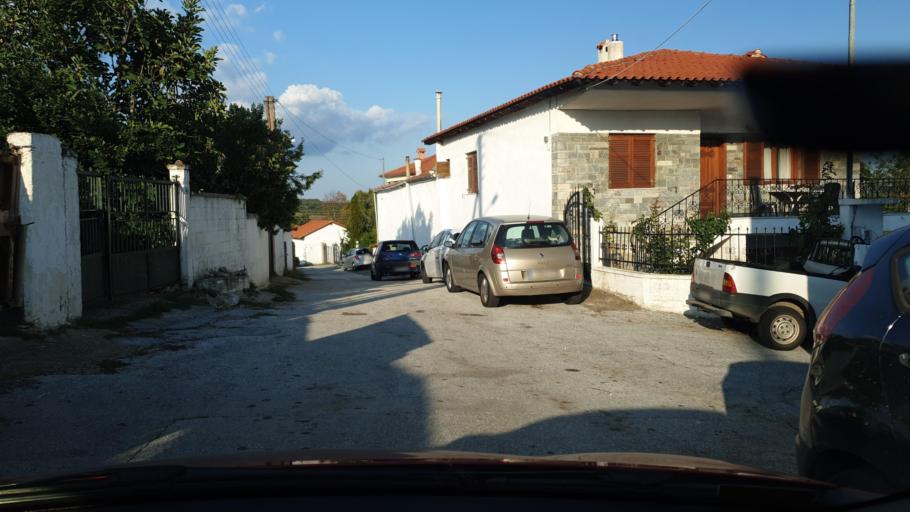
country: GR
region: Central Macedonia
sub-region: Nomos Chalkidikis
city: Galatista
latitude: 40.5166
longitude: 23.2833
